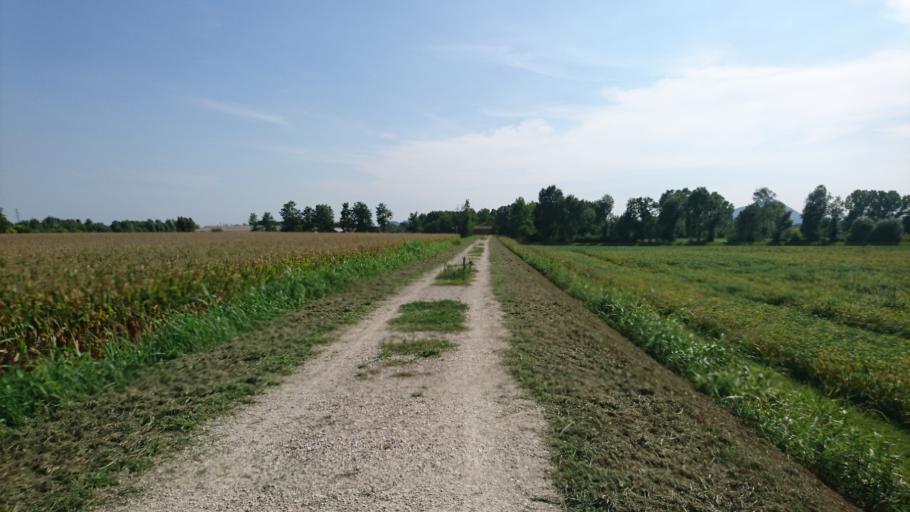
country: IT
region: Veneto
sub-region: Provincia di Padova
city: Veggiano
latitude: 45.4376
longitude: 11.7267
